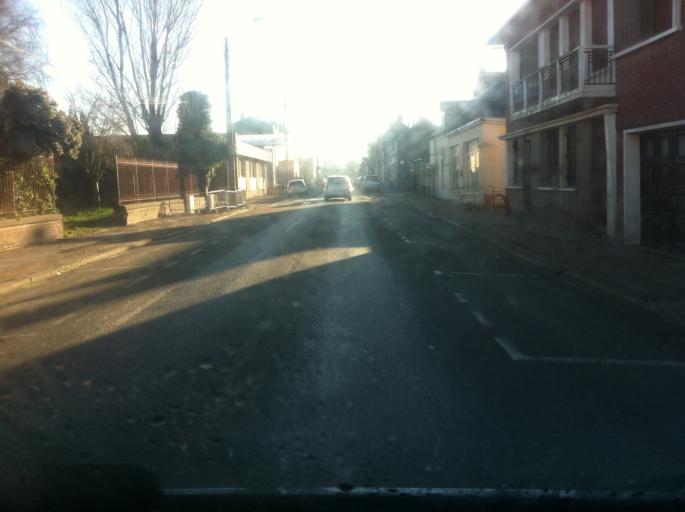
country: FR
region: Haute-Normandie
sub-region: Departement de la Seine-Maritime
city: Le Treport
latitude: 50.0583
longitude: 1.3831
